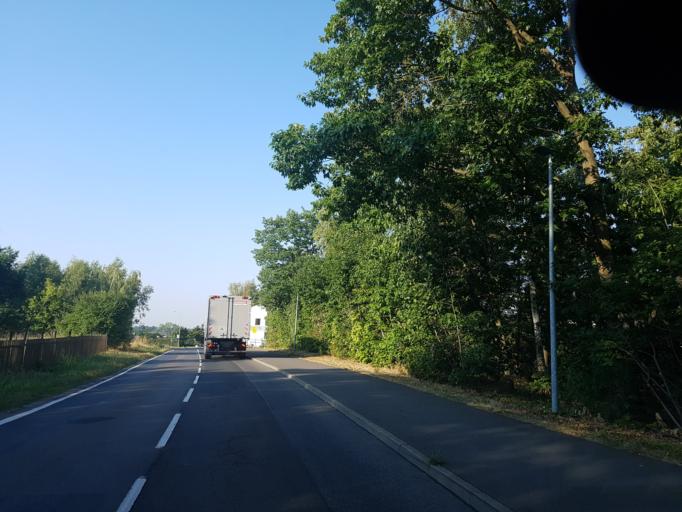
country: DE
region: Brandenburg
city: Elsterwerda
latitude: 51.4711
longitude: 13.5428
